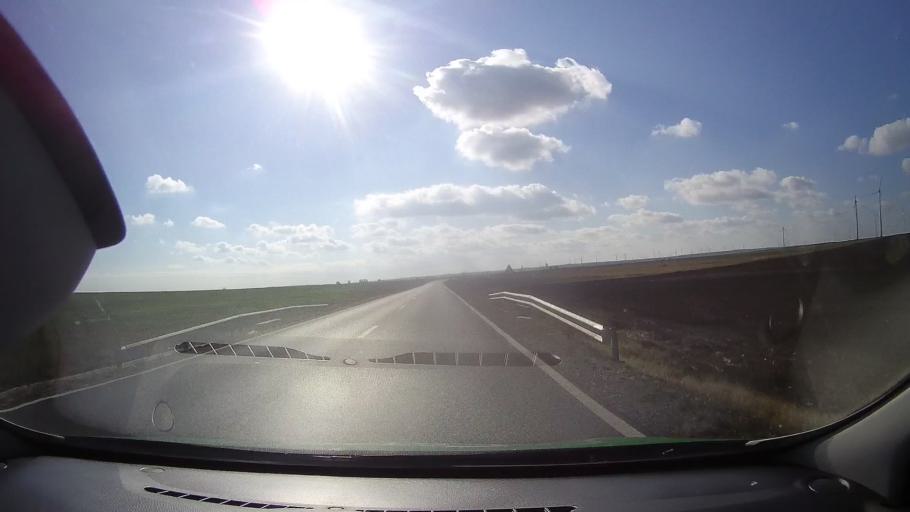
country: RO
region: Constanta
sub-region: Comuna Mihai Viteazu
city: Mihai Viteazu
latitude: 44.6700
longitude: 28.6835
